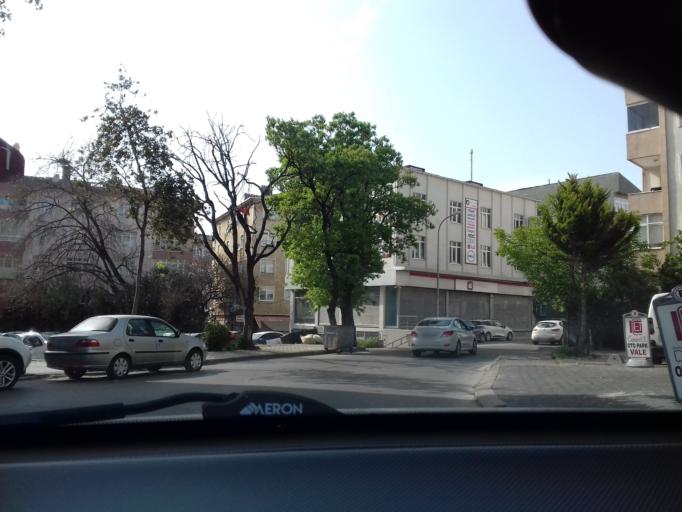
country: TR
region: Istanbul
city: Maltepe
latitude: 40.9159
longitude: 29.2065
